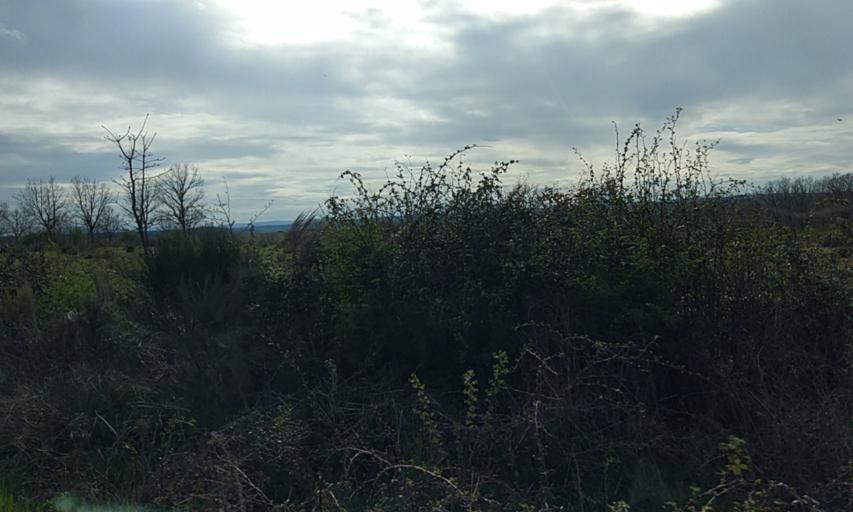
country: ES
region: Castille and Leon
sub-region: Provincia de Salamanca
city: Robleda
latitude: 40.4190
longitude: -6.6009
